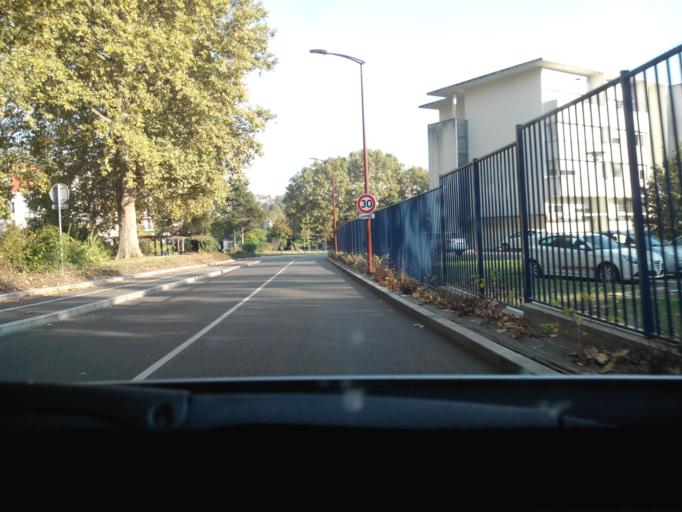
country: FR
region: Ile-de-France
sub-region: Departement du Val-de-Marne
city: Cachan
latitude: 48.7914
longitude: 2.3301
